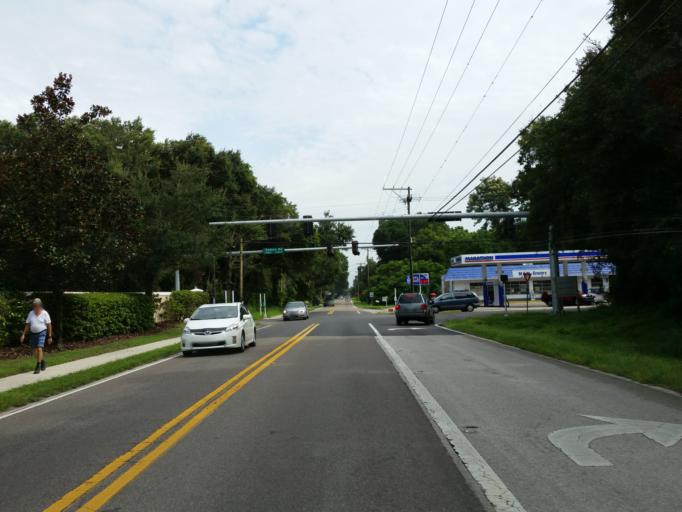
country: US
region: Florida
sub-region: Hillsborough County
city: Seffner
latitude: 27.9666
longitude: -82.2528
